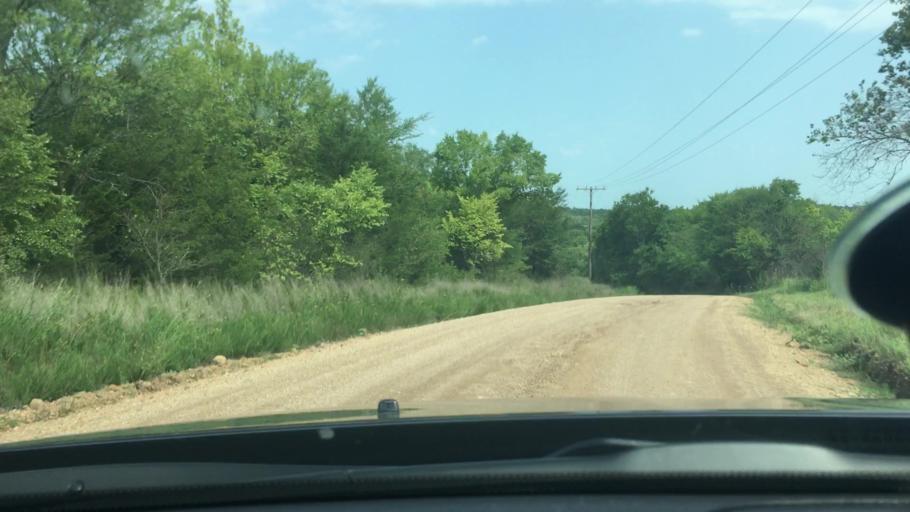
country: US
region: Oklahoma
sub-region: Atoka County
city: Atoka
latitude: 34.4401
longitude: -96.0644
